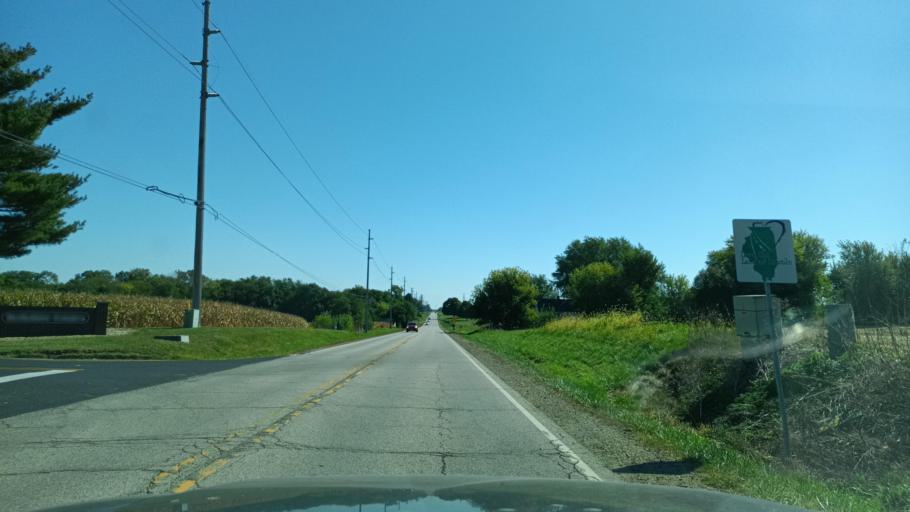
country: US
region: Illinois
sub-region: Peoria County
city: Dunlap
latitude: 40.7839
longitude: -89.7144
